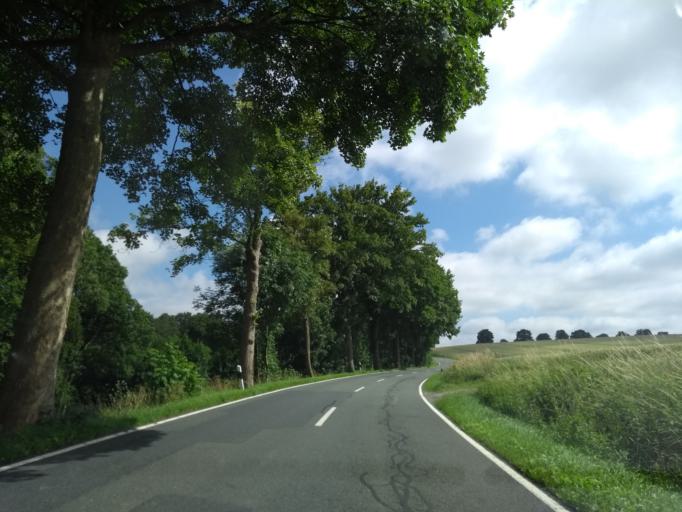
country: DE
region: Lower Saxony
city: Bad Pyrmont
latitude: 51.9654
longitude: 9.3051
